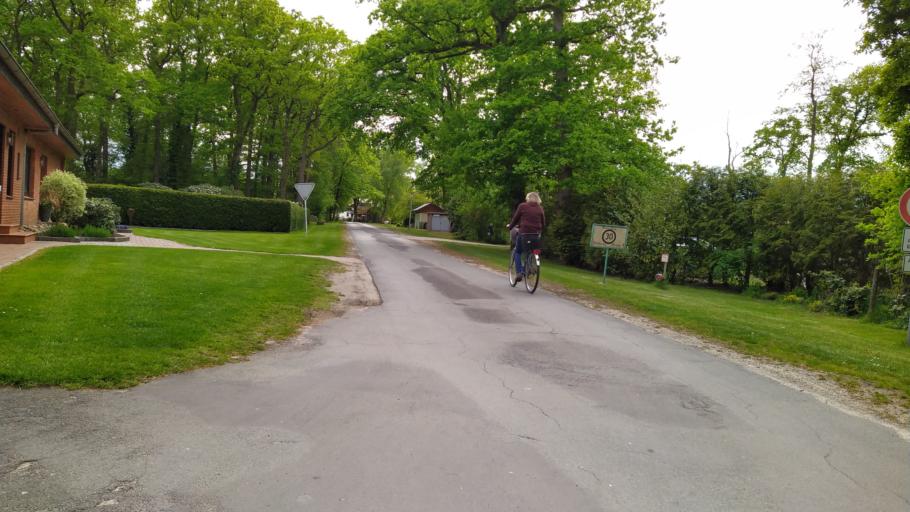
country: DE
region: Lower Saxony
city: Brest
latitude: 53.4338
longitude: 9.3523
